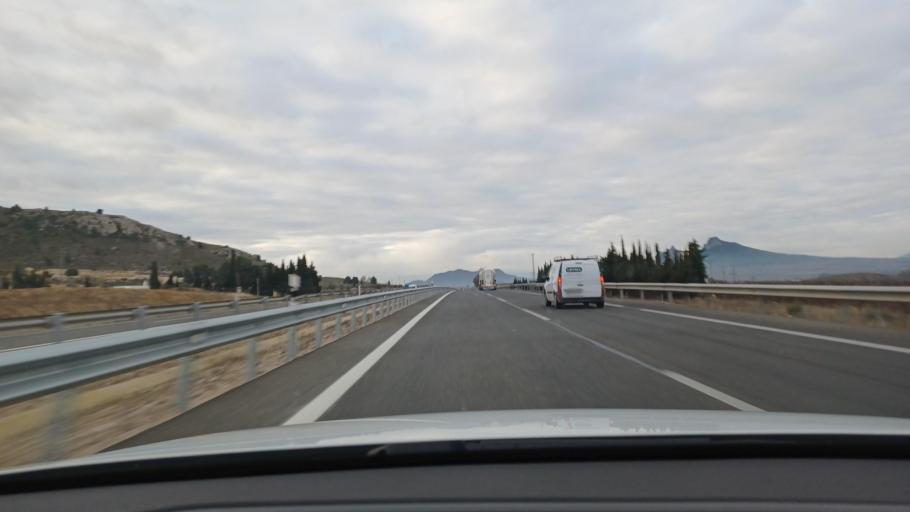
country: ES
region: Valencia
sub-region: Provincia de Alicante
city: Villena
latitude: 38.5939
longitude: -0.8443
